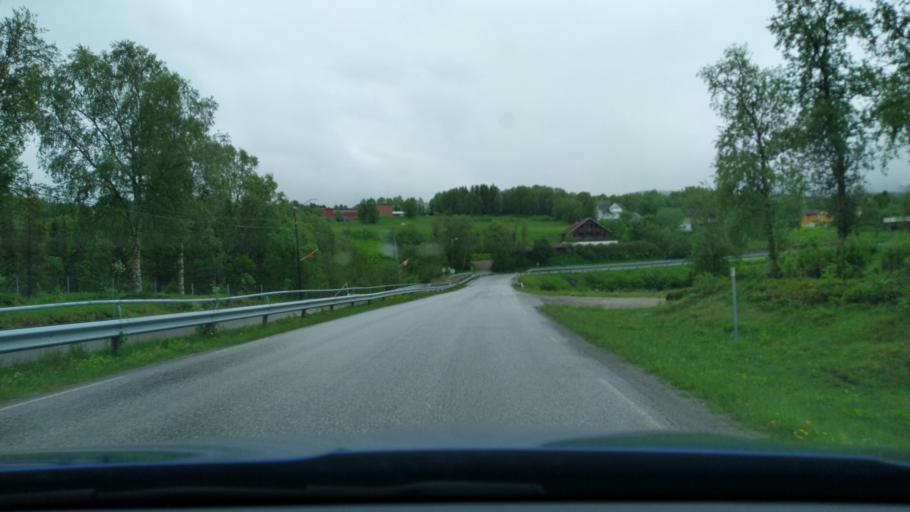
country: NO
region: Troms
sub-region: Dyroy
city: Brostadbotn
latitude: 69.0875
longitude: 17.6953
